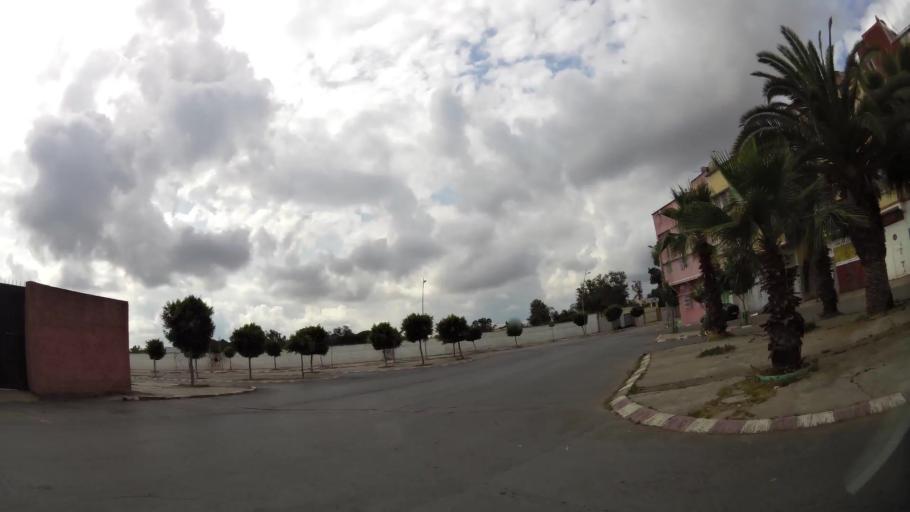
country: MA
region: Gharb-Chrarda-Beni Hssen
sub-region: Kenitra Province
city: Kenitra
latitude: 34.2585
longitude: -6.5672
